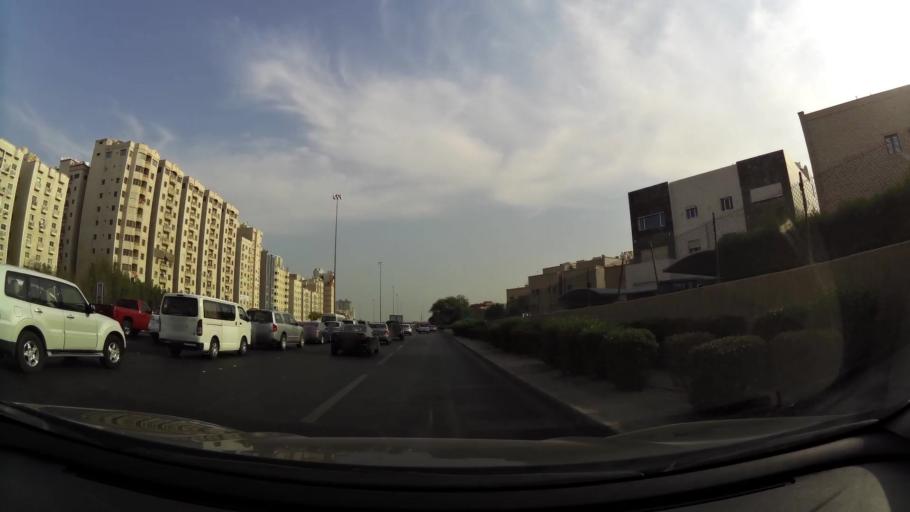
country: KW
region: Muhafazat Hawalli
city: Hawalli
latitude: 29.3278
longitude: 48.0086
